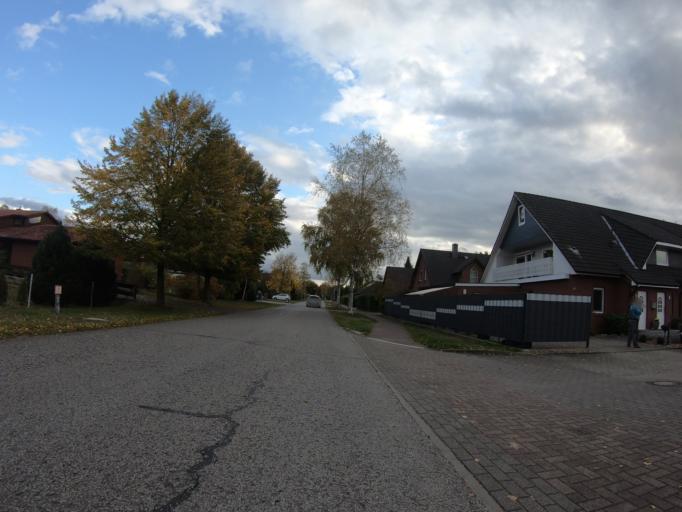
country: DE
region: Lower Saxony
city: Wagenhoff
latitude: 52.5543
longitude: 10.5262
